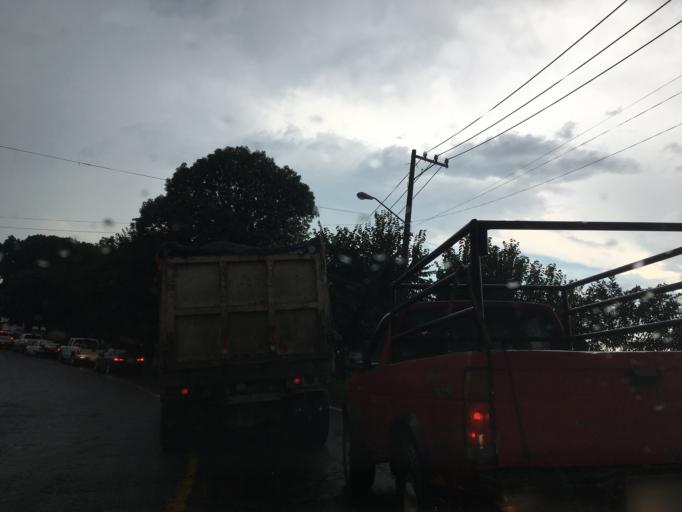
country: MX
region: Michoacan
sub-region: Uruapan
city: Uruapan
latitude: 19.4343
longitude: -102.0765
